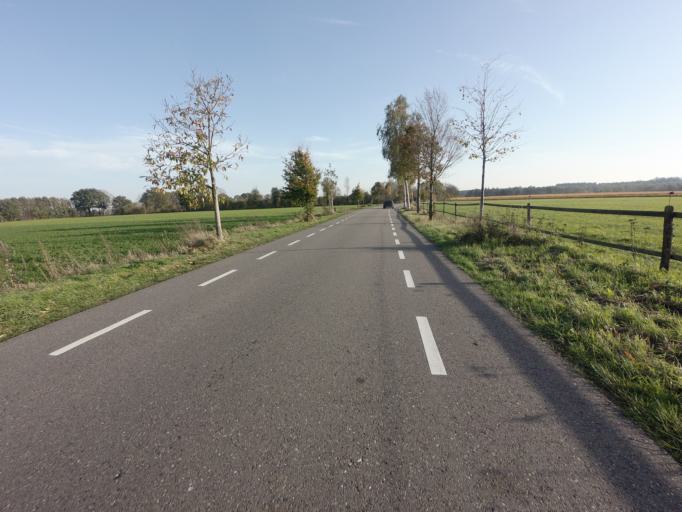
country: DE
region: North Rhine-Westphalia
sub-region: Regierungsbezirk Koln
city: Waldfeucht
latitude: 51.1048
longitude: 5.9852
